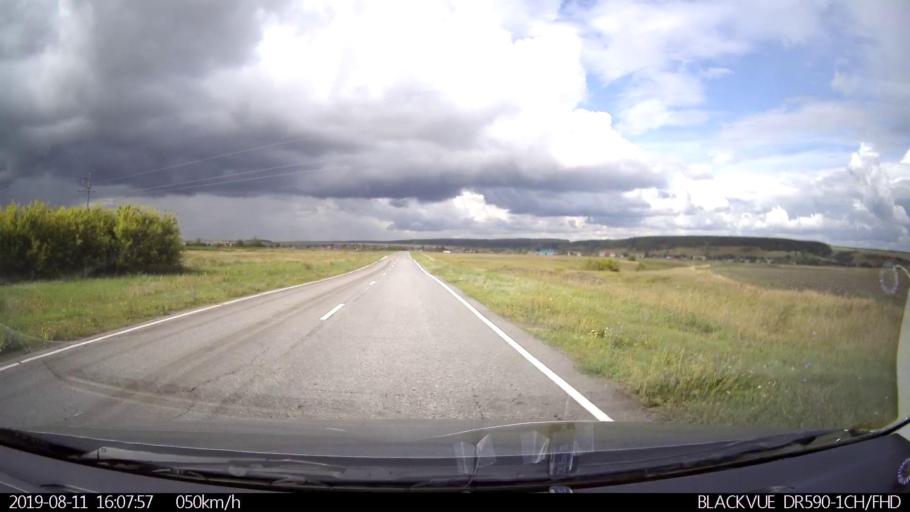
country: RU
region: Ulyanovsk
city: Ignatovka
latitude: 53.9810
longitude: 47.6471
